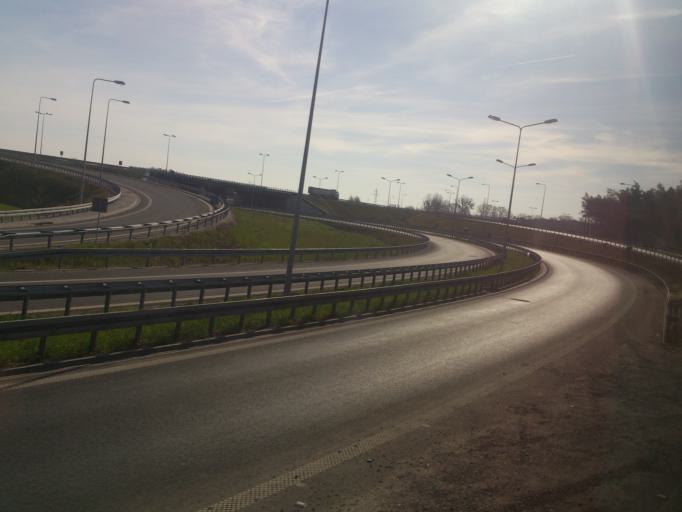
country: PL
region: Kujawsko-Pomorskie
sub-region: Powiat aleksandrowski
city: Ciechocinek
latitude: 52.8662
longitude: 18.7567
